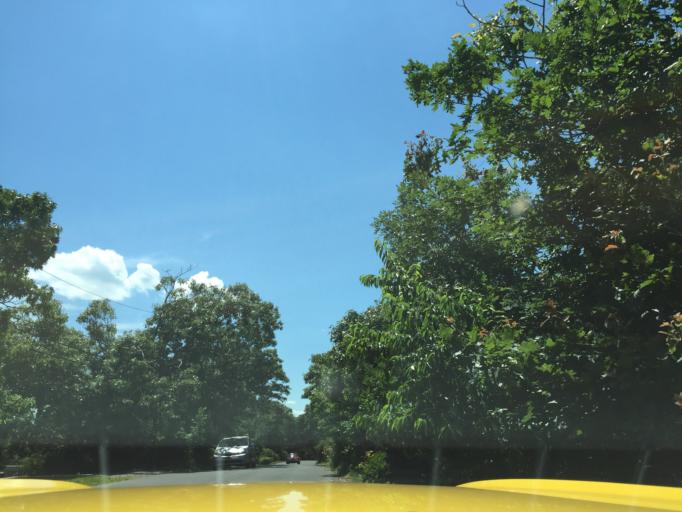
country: US
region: New York
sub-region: Suffolk County
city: Montauk
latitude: 41.0146
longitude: -72.0010
